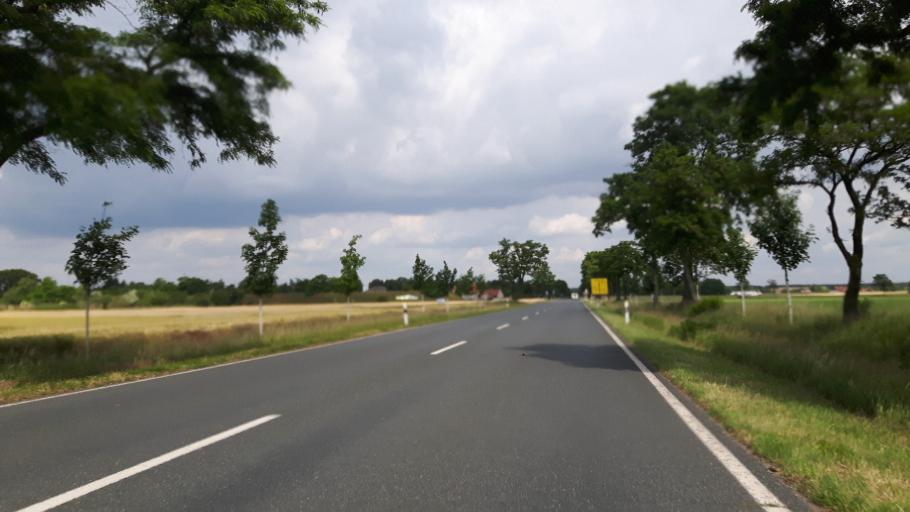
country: DE
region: Saxony-Anhalt
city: Schlaitz
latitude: 51.6548
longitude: 12.4370
